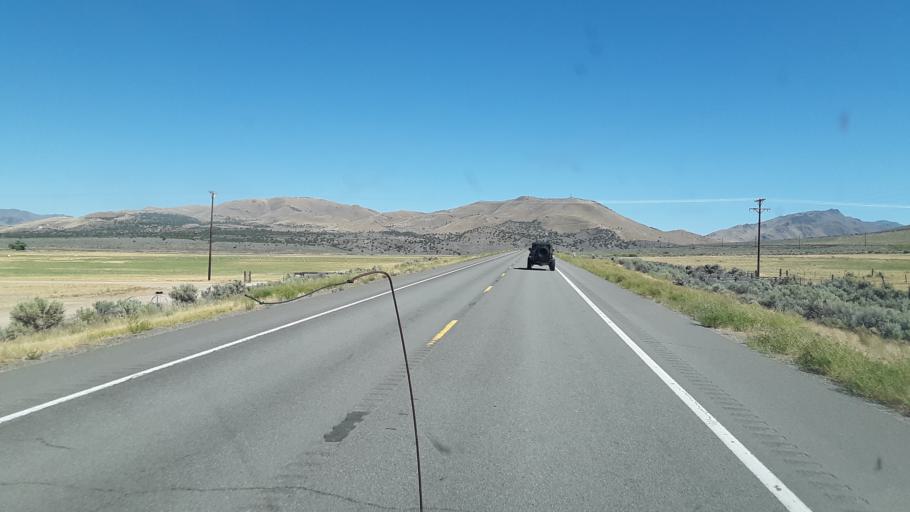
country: US
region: Nevada
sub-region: Washoe County
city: Cold Springs
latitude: 39.9547
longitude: -120.0355
